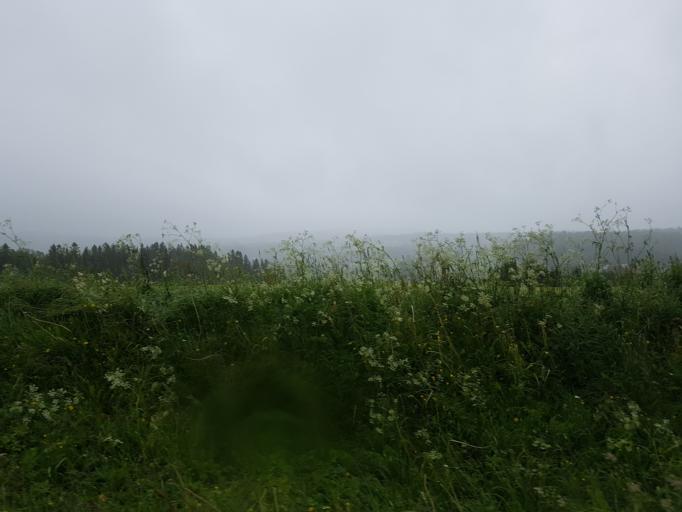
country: NO
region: Sor-Trondelag
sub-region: Selbu
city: Mebonden
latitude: 63.3841
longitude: 11.0805
